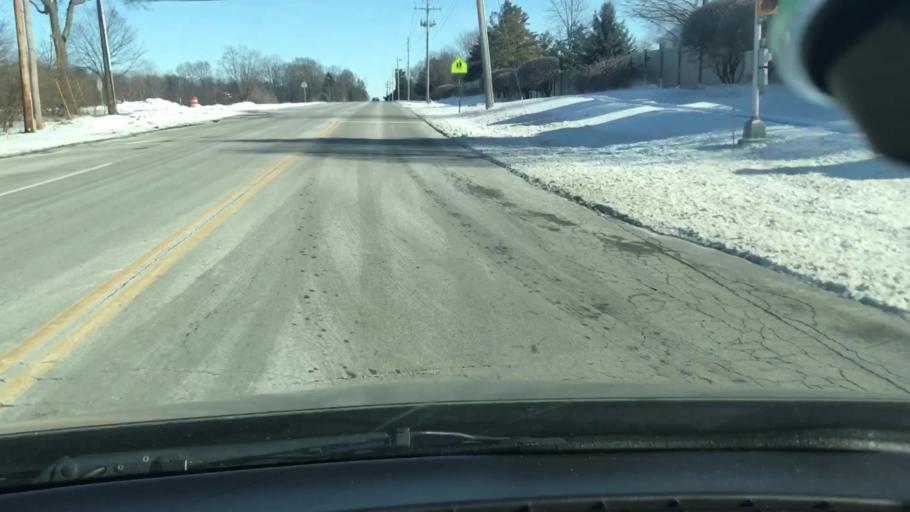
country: US
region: Indiana
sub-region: Hamilton County
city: Carmel
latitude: 39.9711
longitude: -86.0851
